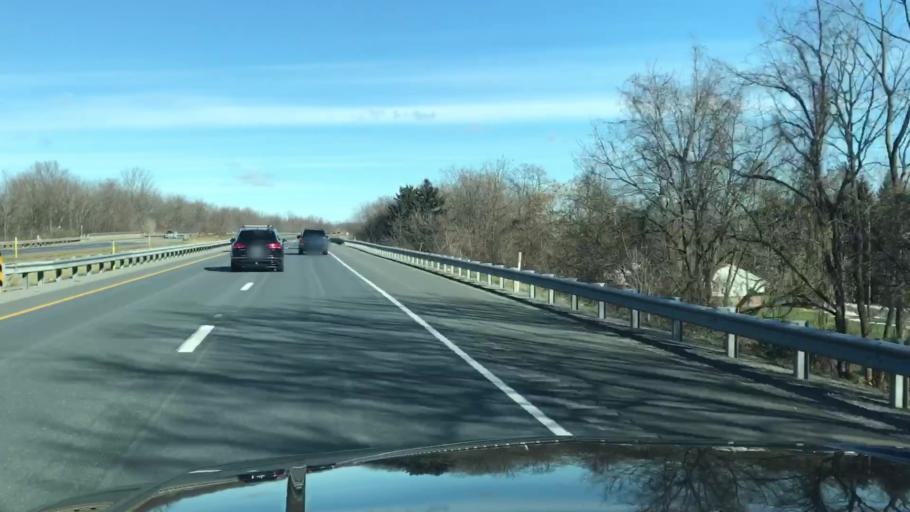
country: US
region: Pennsylvania
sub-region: Snyder County
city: Selinsgrove
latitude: 40.7975
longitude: -76.8585
